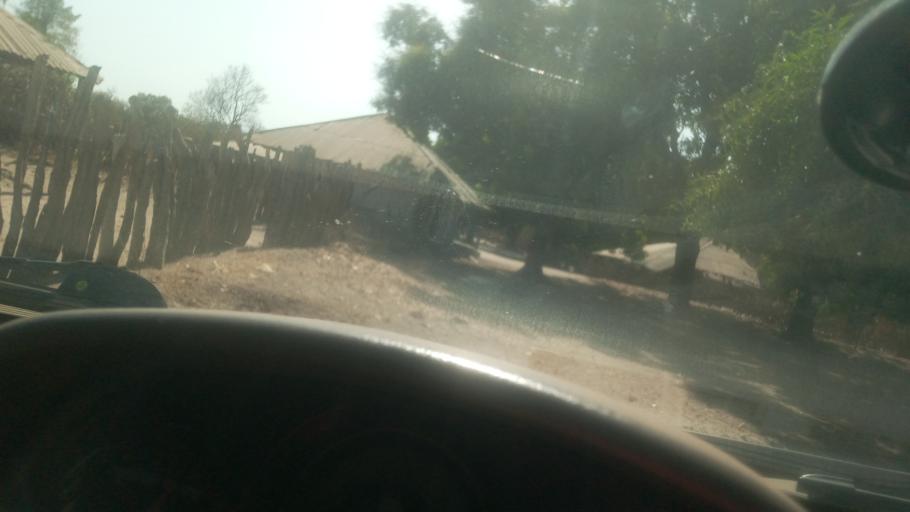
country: GW
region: Oio
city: Farim
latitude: 12.4515
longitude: -15.4244
